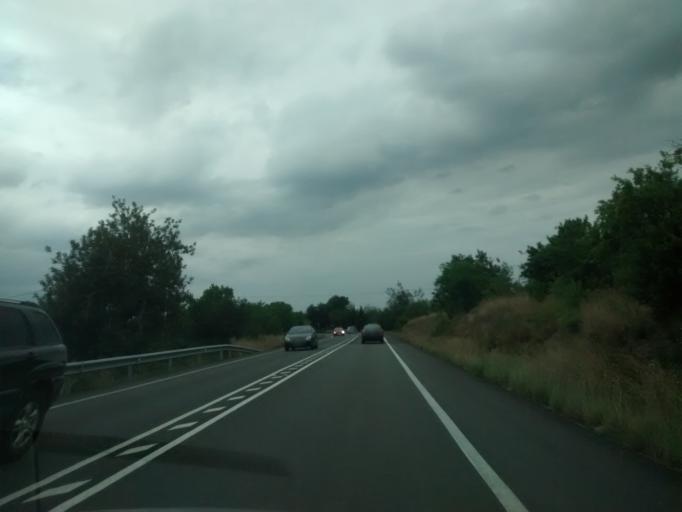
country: ES
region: Catalonia
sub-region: Provincia de Tarragona
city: Tortosa
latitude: 40.8536
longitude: 0.5118
